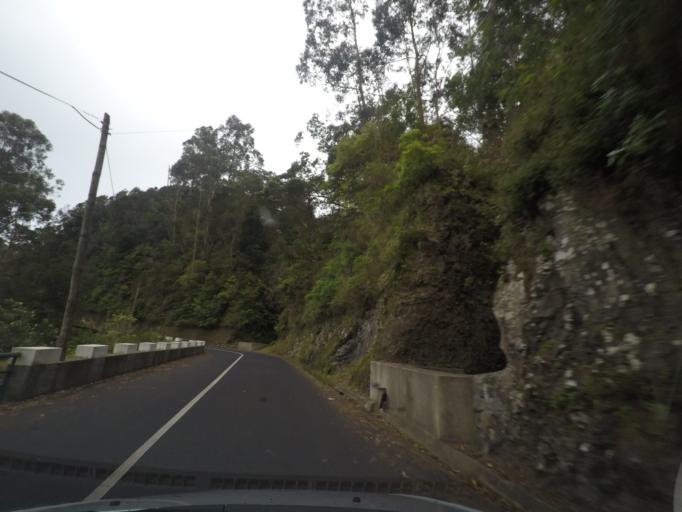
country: PT
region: Madeira
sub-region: Santa Cruz
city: Camacha
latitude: 32.7487
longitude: -16.8329
